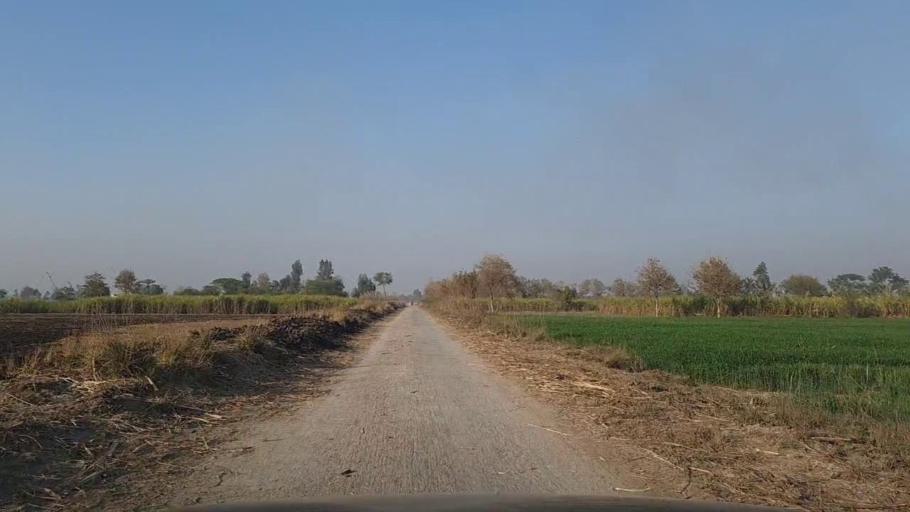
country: PK
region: Sindh
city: Daur
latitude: 26.4574
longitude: 68.4379
